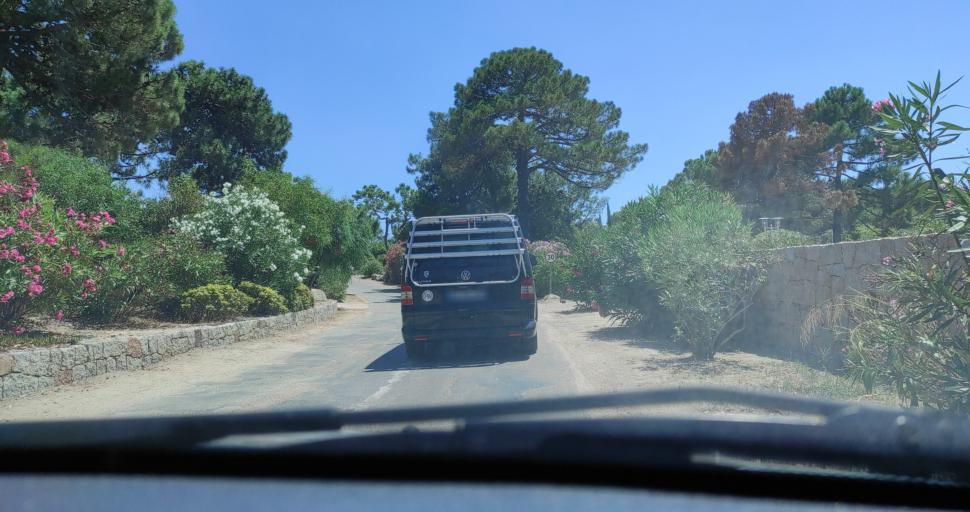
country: FR
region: Corsica
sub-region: Departement de la Corse-du-Sud
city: Porto-Vecchio
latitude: 41.6218
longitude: 9.3394
